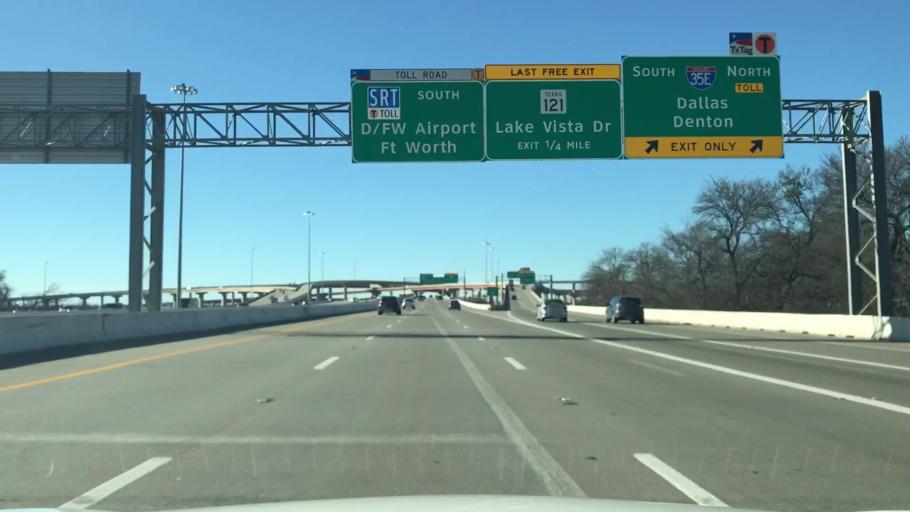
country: US
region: Texas
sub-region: Denton County
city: Lewisville
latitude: 33.0052
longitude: -96.9523
